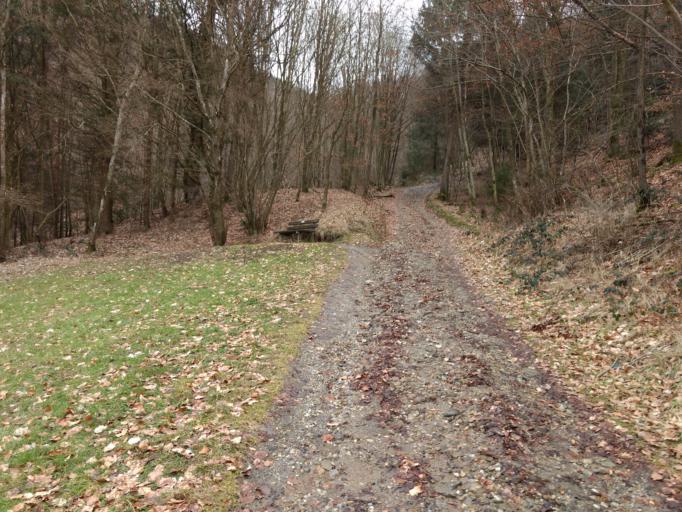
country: AT
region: Upper Austria
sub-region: Politischer Bezirk Rohrbach
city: Atzesberg
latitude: 48.4245
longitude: 13.8739
